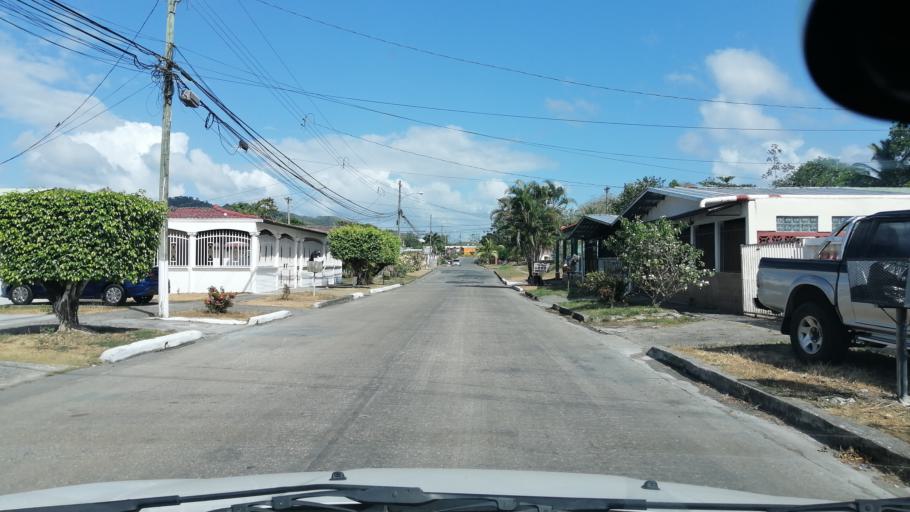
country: PA
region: Panama
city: Alcalde Diaz
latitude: 9.1395
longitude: -79.5519
